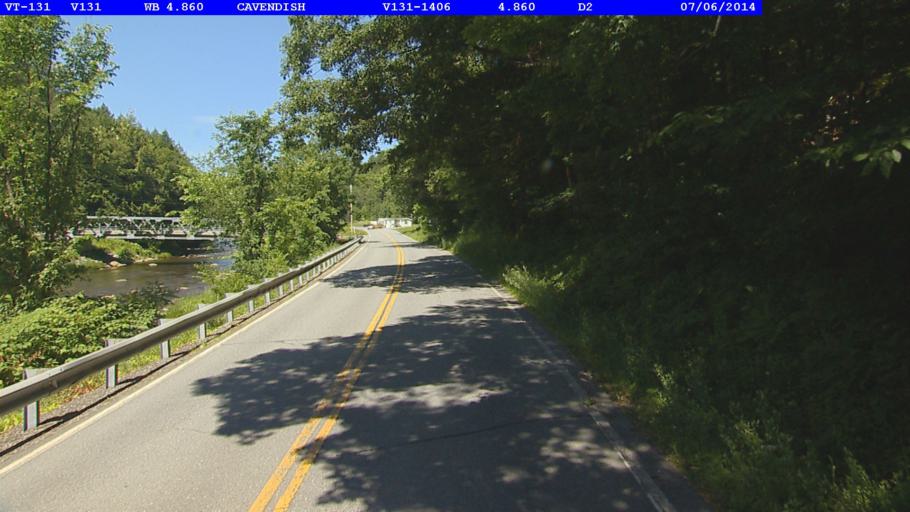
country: US
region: Vermont
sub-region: Windsor County
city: Springfield
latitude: 43.4044
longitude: -72.5740
